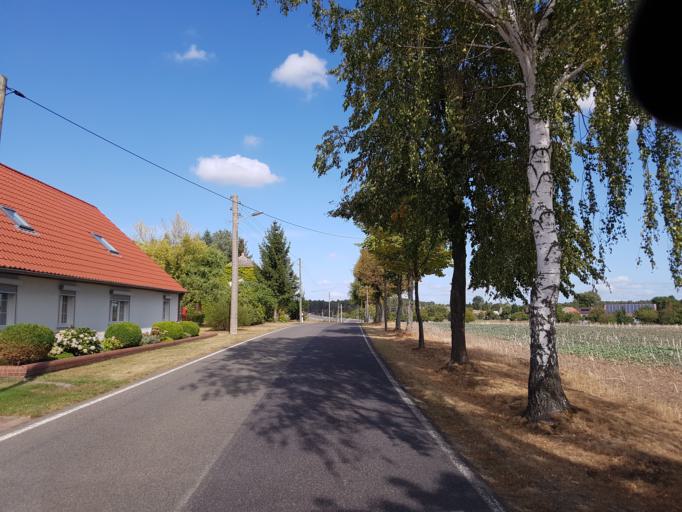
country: DE
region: Brandenburg
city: Sonnewalde
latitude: 51.7517
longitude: 13.6147
